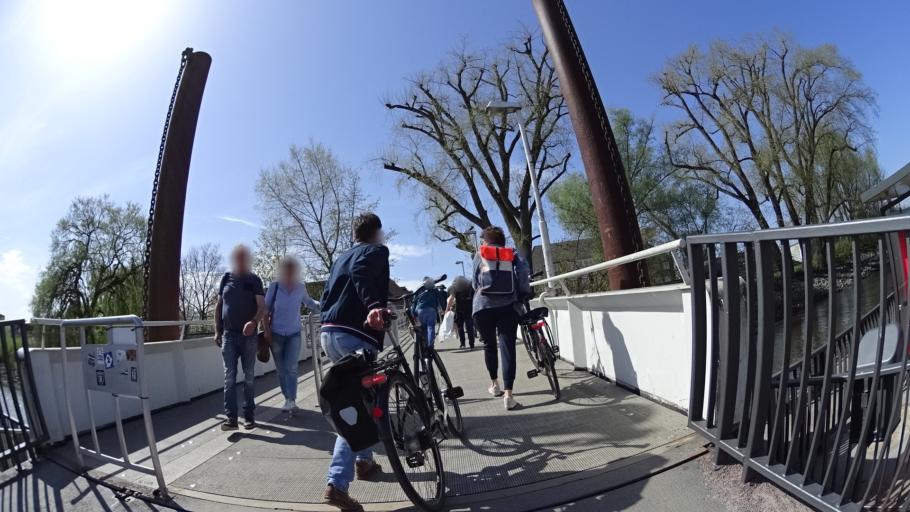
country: DE
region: Hamburg
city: Altona
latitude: 53.5364
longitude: 9.8789
